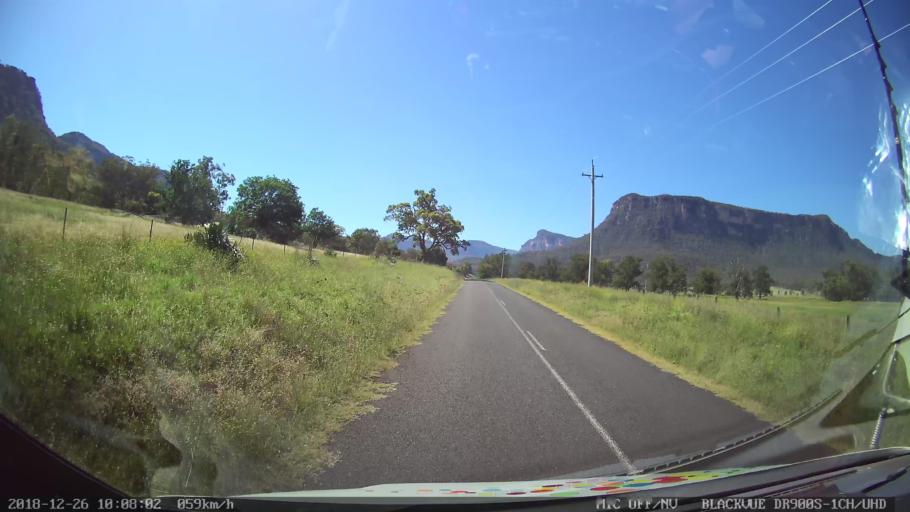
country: AU
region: New South Wales
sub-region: Mid-Western Regional
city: Kandos
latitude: -33.0945
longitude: 150.2281
